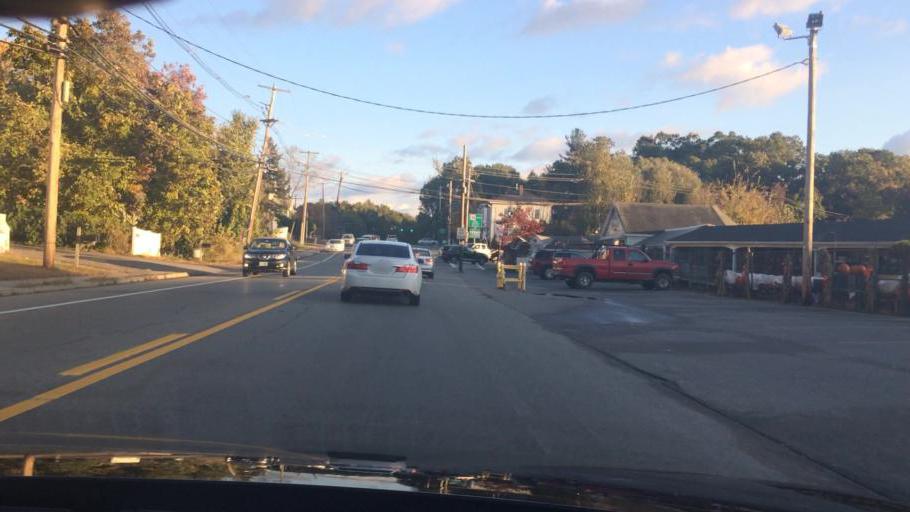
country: US
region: Massachusetts
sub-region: Middlesex County
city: Chelmsford
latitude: 42.6329
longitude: -71.3759
